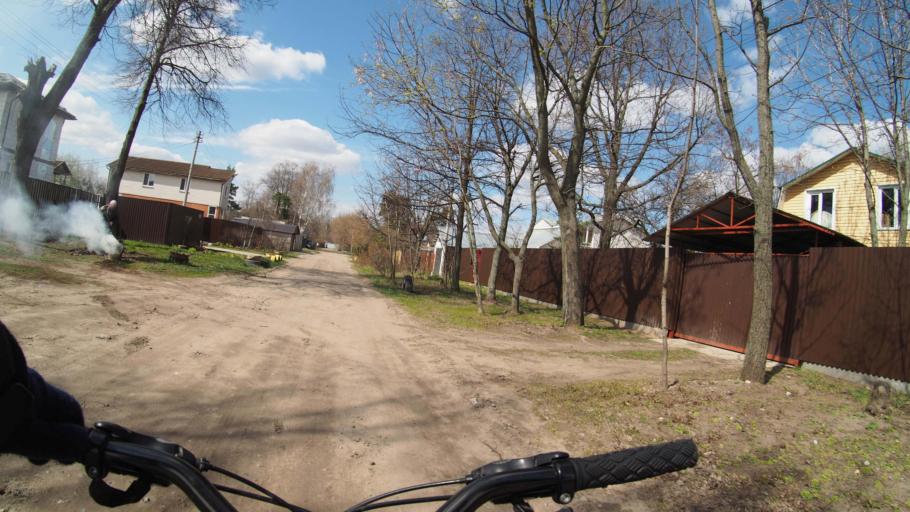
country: RU
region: Moskovskaya
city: Ramenskoye
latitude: 55.5614
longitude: 38.2330
